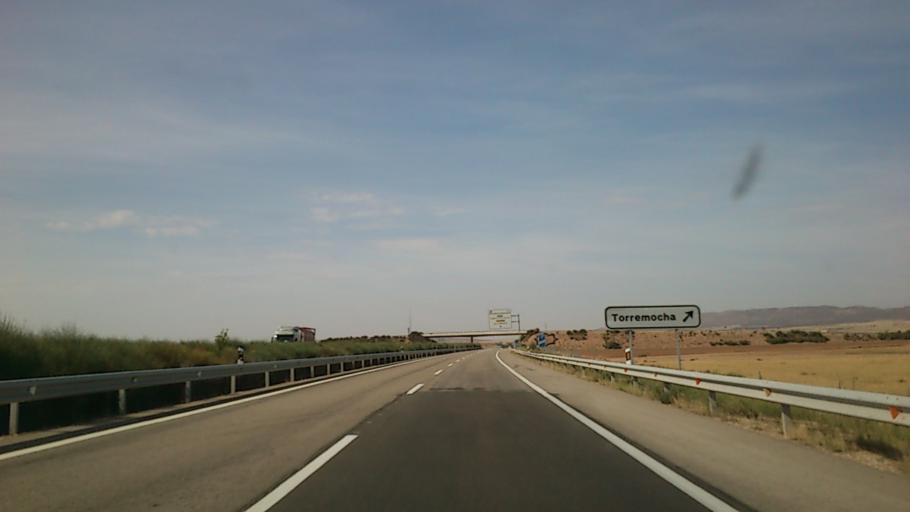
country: ES
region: Aragon
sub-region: Provincia de Teruel
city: Santa Eulalia
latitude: 40.5620
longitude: -1.2788
